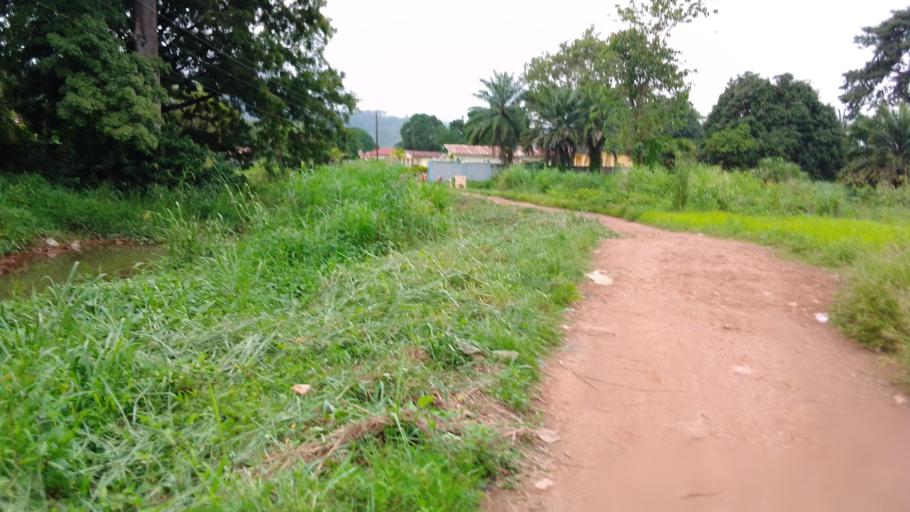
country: SL
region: Eastern Province
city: Kenema
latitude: 7.8605
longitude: -11.2017
